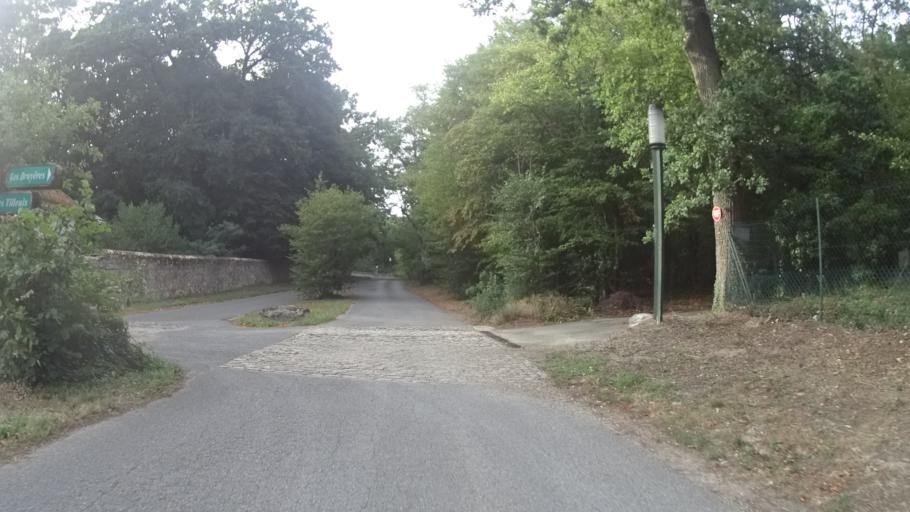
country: FR
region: Picardie
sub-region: Departement de l'Oise
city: Ver-sur-Launette
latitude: 49.1306
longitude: 2.7008
